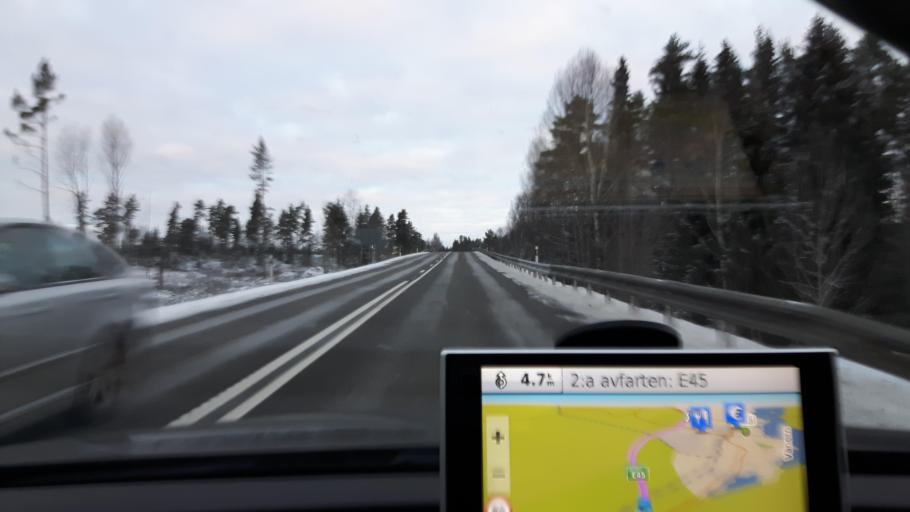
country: SE
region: Vaestra Goetaland
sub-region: Amals Kommun
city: Amal
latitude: 59.0167
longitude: 12.6902
